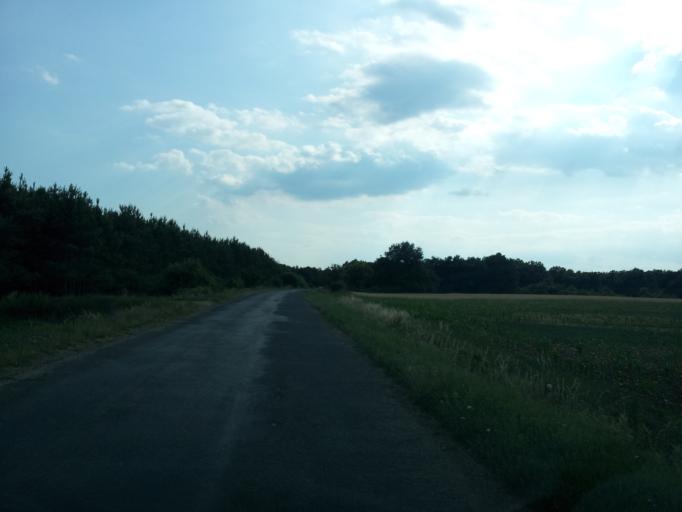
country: HU
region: Veszprem
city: Zanka
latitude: 46.9683
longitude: 17.6675
